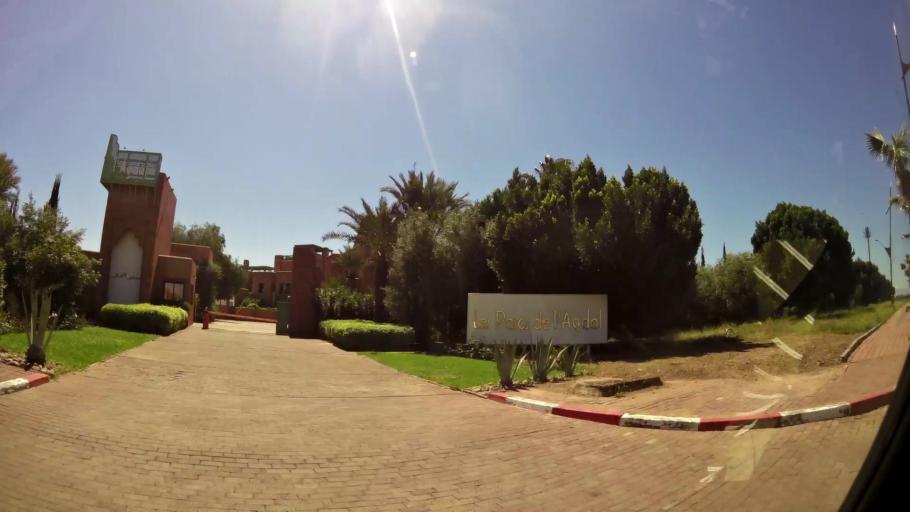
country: MA
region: Marrakech-Tensift-Al Haouz
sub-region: Marrakech
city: Marrakesh
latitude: 31.5999
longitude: -8.0015
